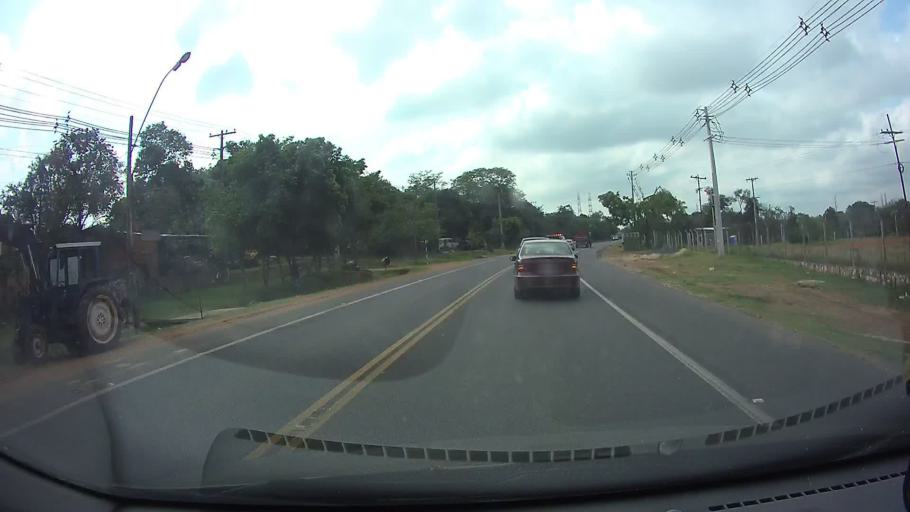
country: PY
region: Central
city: Limpio
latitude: -25.1407
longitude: -57.4561
